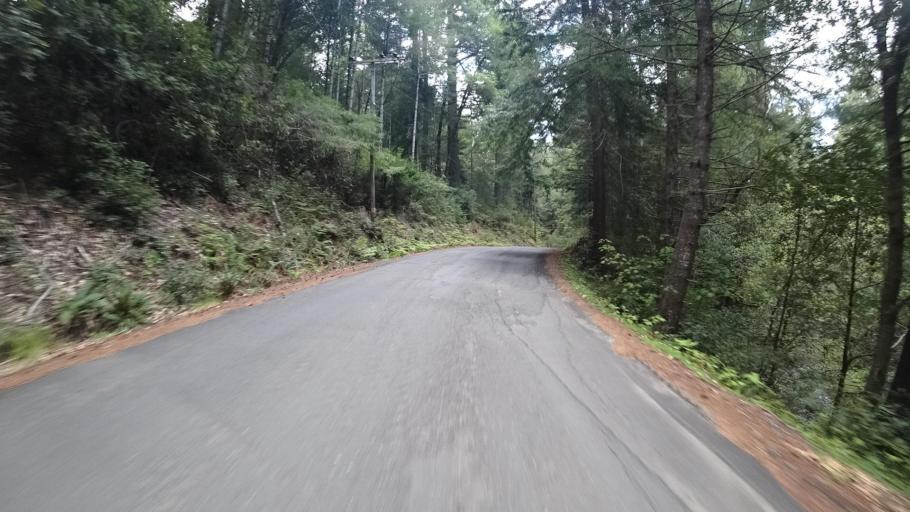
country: US
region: California
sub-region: Humboldt County
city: Redway
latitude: 40.0023
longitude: -123.9281
